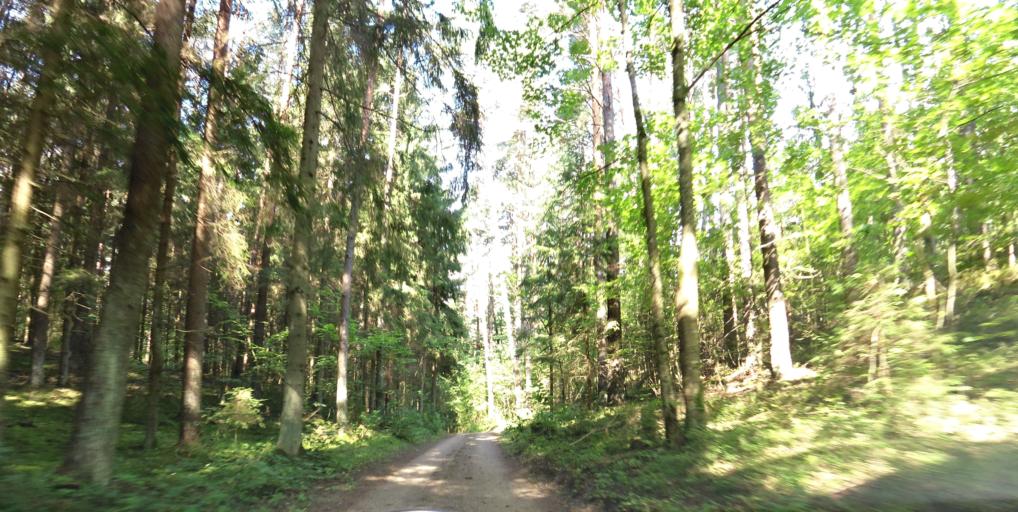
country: LT
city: Grigiskes
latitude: 54.7388
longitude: 25.0396
